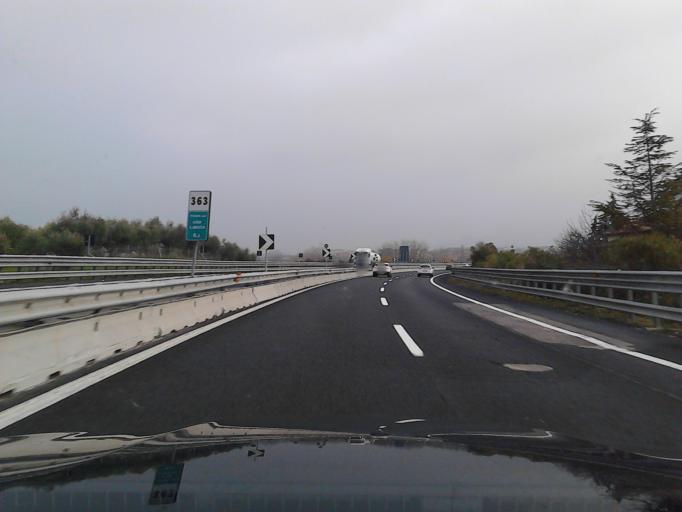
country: IT
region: Abruzzo
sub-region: Provincia di Pescara
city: San Martino Bassa
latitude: 42.5288
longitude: 14.1308
